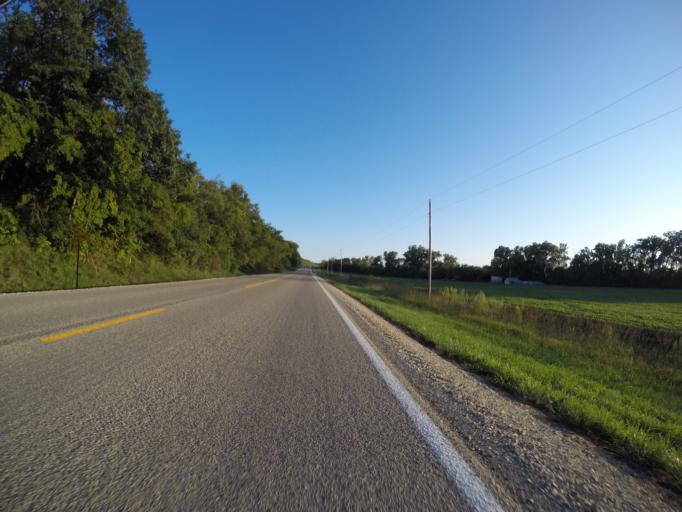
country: US
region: Kansas
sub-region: Riley County
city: Manhattan
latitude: 39.1498
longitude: -96.5579
